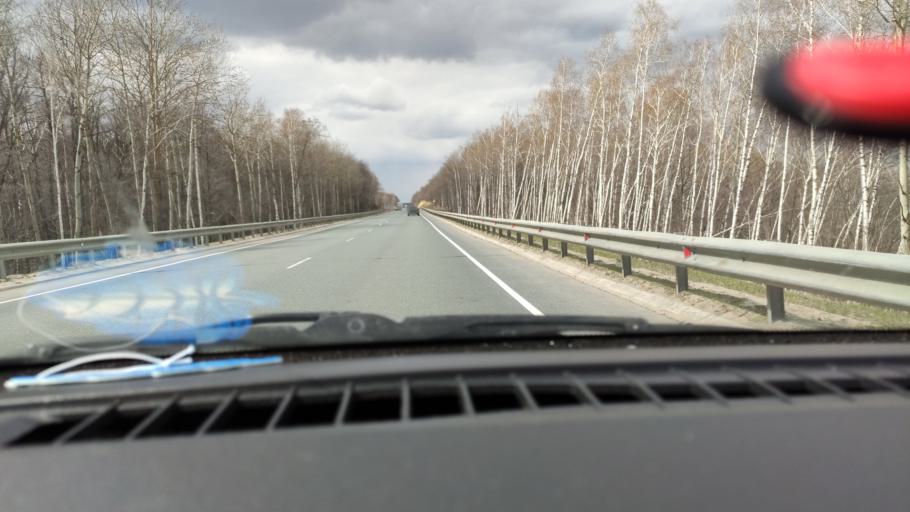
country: RU
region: Saratov
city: Vol'sk
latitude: 52.1113
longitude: 47.3381
